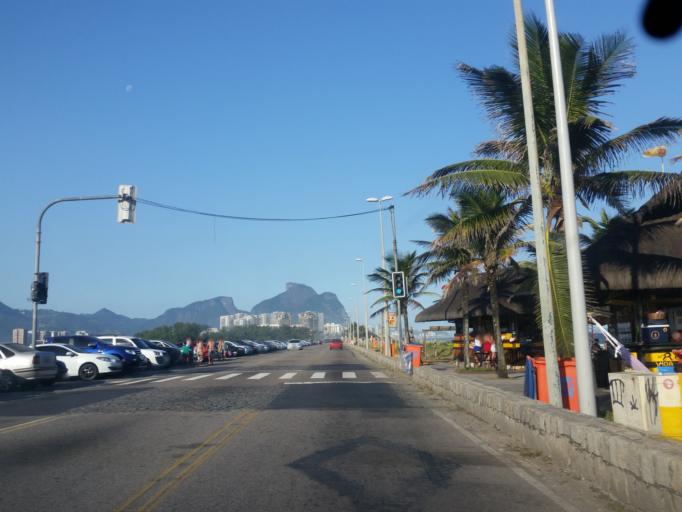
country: BR
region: Rio de Janeiro
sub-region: Nilopolis
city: Nilopolis
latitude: -23.0123
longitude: -43.3846
